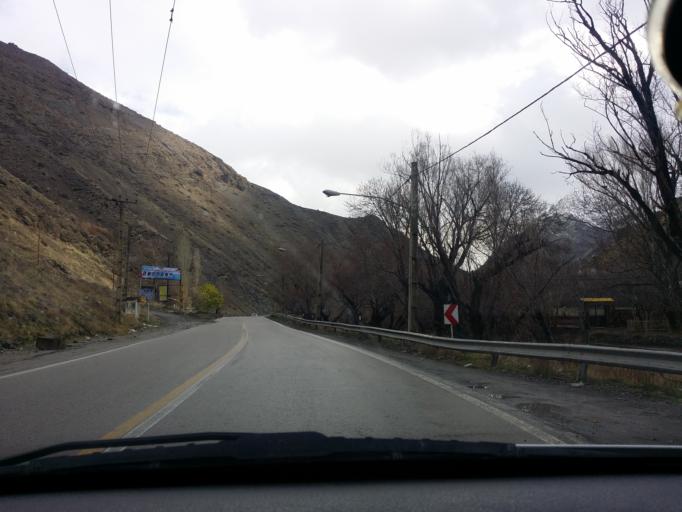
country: IR
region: Tehran
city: Tajrish
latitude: 36.0313
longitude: 51.2313
